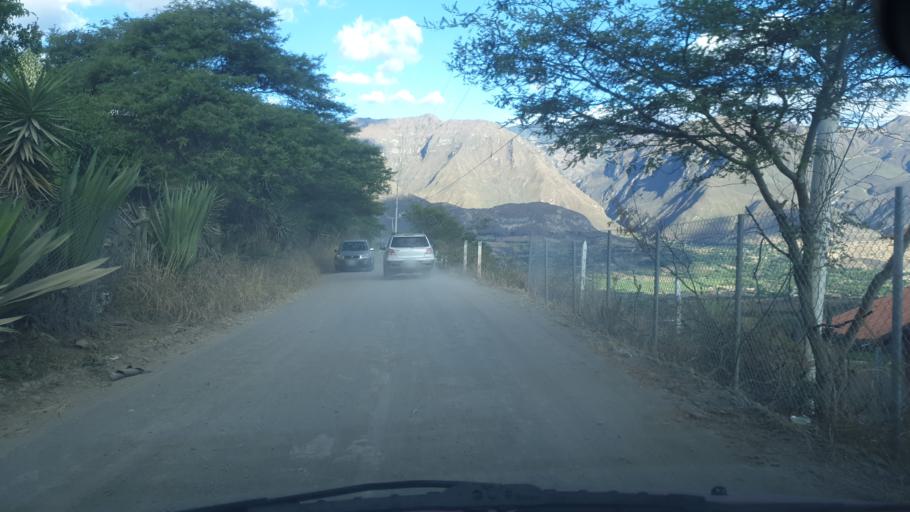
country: EC
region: Azuay
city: Cuenca
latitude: -3.2846
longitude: -79.2972
